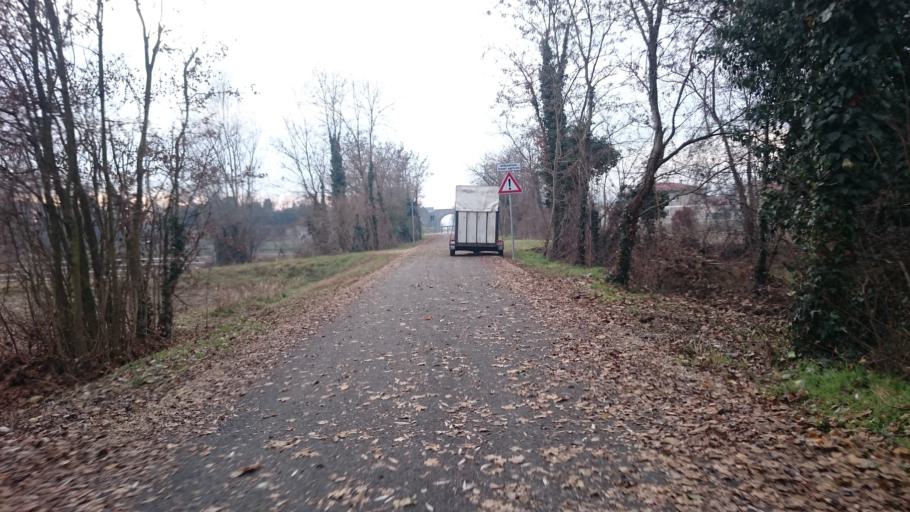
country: IT
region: Veneto
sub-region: Provincia di Vicenza
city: Grisignano di Zocco
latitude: 45.4846
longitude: 11.6833
